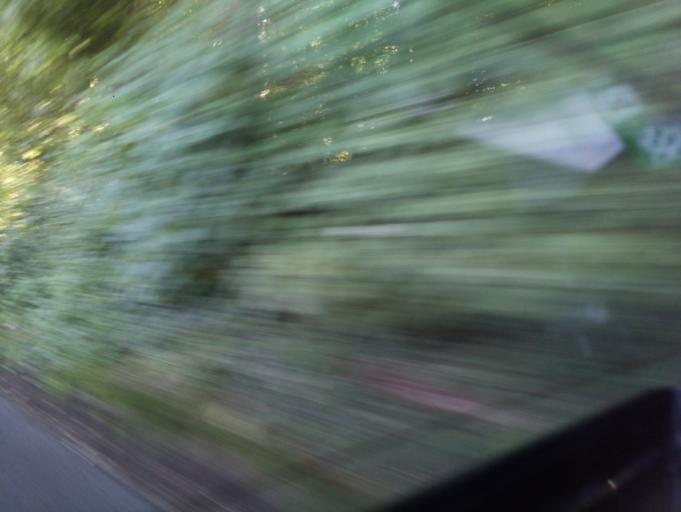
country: GB
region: England
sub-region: Gloucestershire
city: Coleford
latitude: 51.7873
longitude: -2.6478
